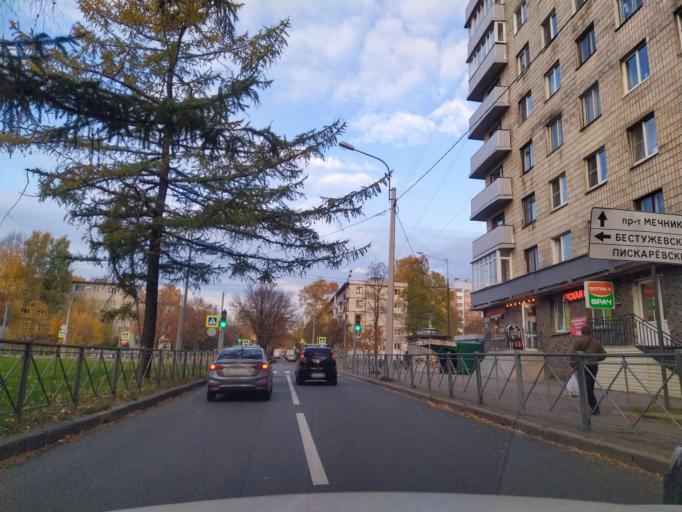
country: RU
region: Leningrad
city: Kalininskiy
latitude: 59.9822
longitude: 30.4087
